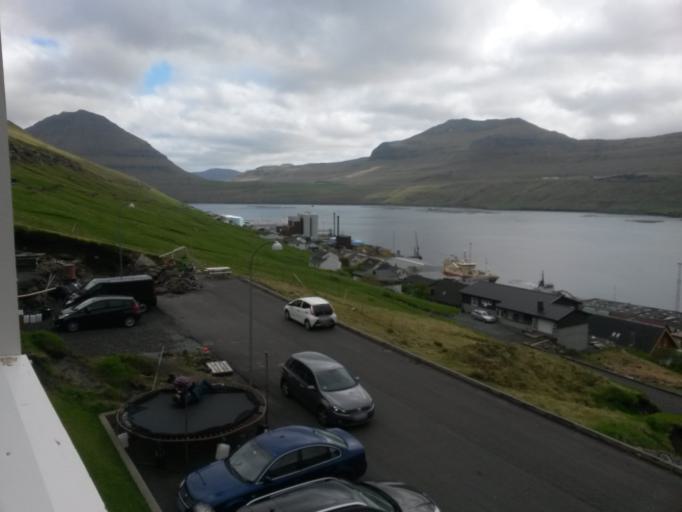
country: FO
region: Eysturoy
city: Fuglafjordur
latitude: 62.2435
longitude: -6.8057
